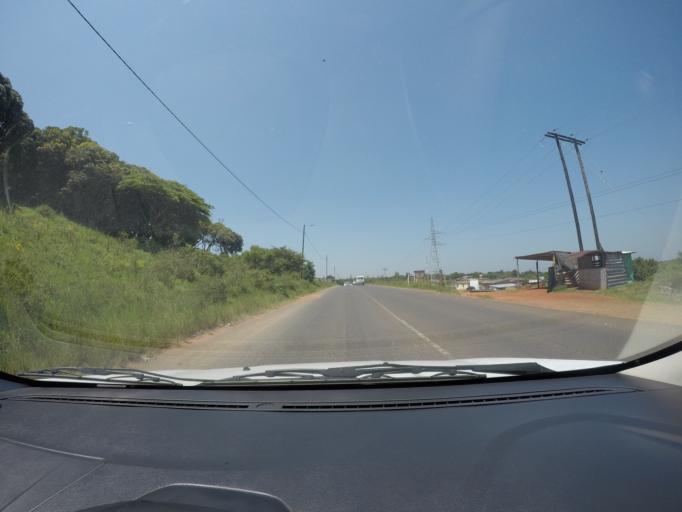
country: ZA
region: KwaZulu-Natal
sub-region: uThungulu District Municipality
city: eSikhawini
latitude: -28.8513
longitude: 31.9255
